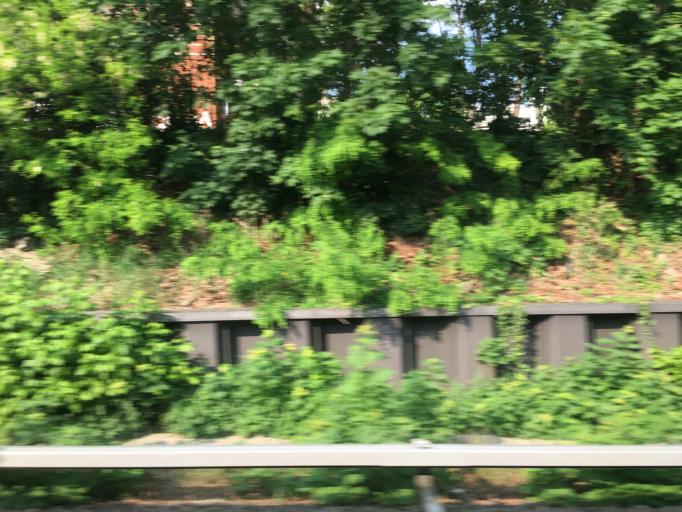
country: DE
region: Berlin
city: Halensee
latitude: 52.4974
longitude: 13.2890
